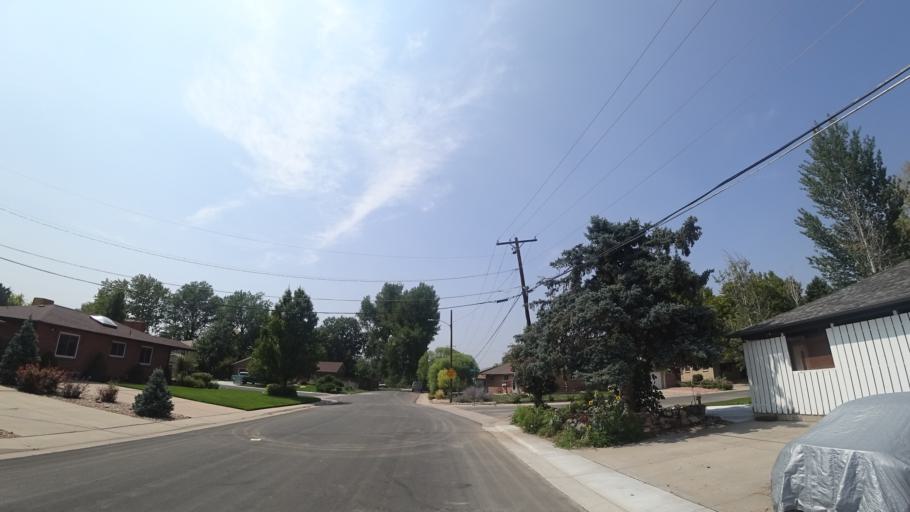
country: US
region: Colorado
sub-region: Arapahoe County
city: Littleton
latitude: 39.6277
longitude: -105.0016
